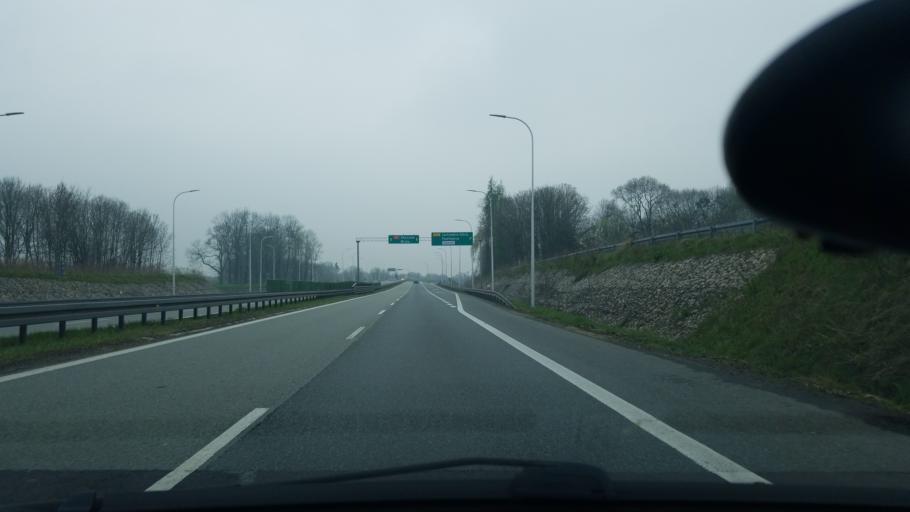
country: PL
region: Silesian Voivodeship
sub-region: Powiat pszczynski
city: Pawlowice
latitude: 49.9545
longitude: 18.7215
